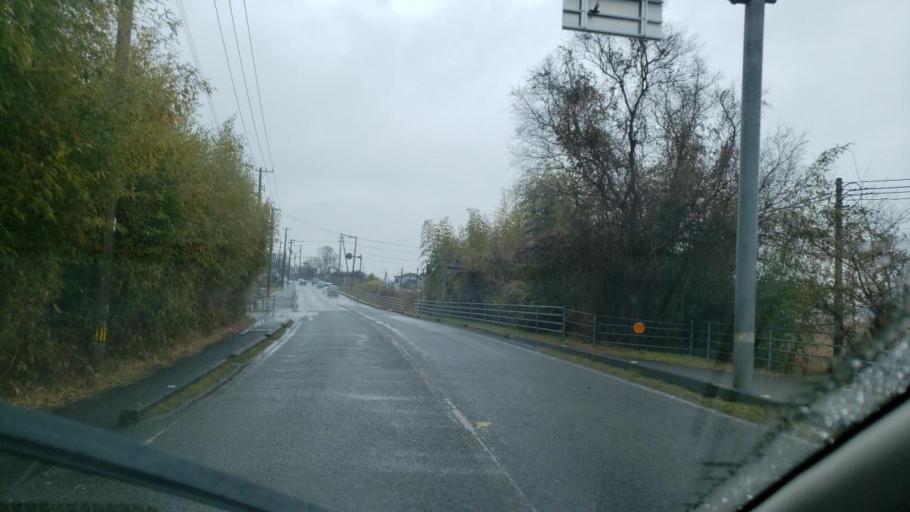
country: JP
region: Tokushima
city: Tokushima-shi
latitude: 34.1554
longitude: 134.5179
